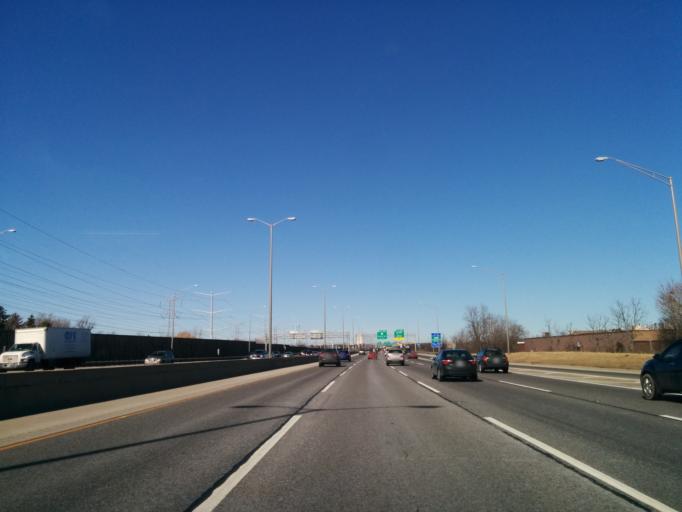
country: US
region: Illinois
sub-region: DuPage County
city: Lisle
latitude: 41.7906
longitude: -88.0565
